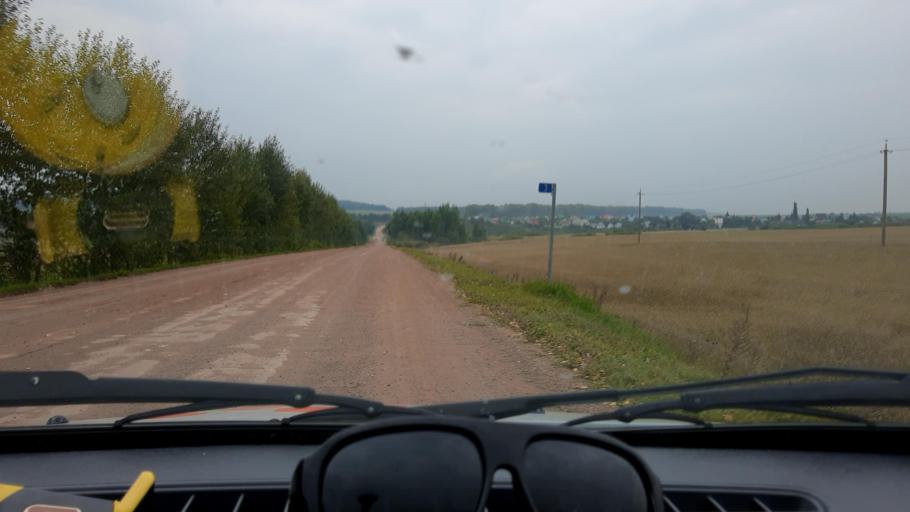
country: RU
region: Bashkortostan
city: Asanovo
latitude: 54.9633
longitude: 55.5988
